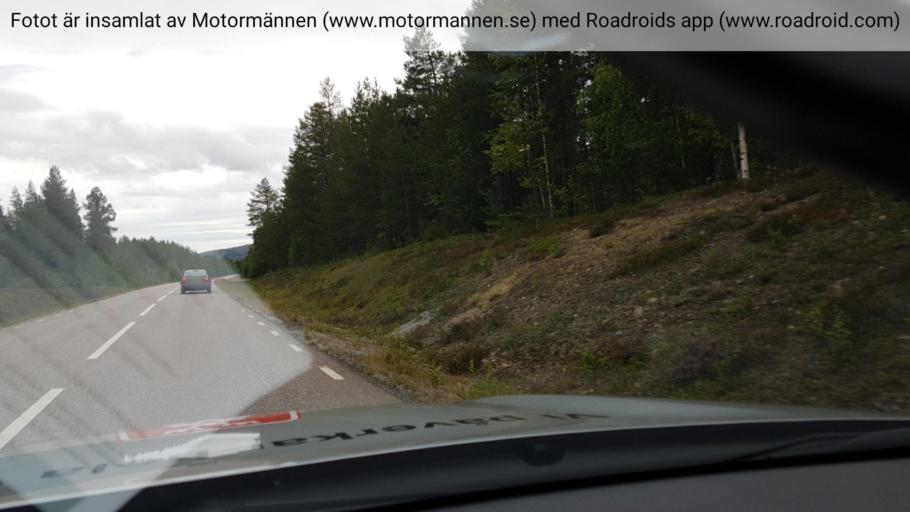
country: SE
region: Norrbotten
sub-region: Overkalix Kommun
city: OEverkalix
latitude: 66.6305
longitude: 22.7831
